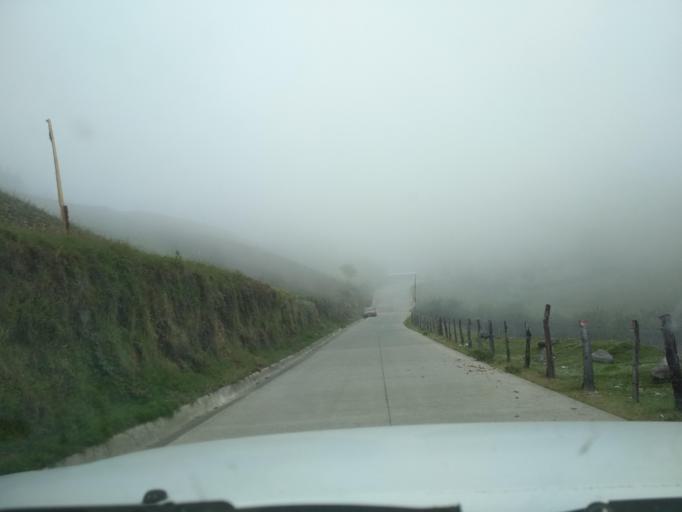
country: MX
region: Veracruz
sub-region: La Perla
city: Chilapa
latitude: 18.9822
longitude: -97.1919
